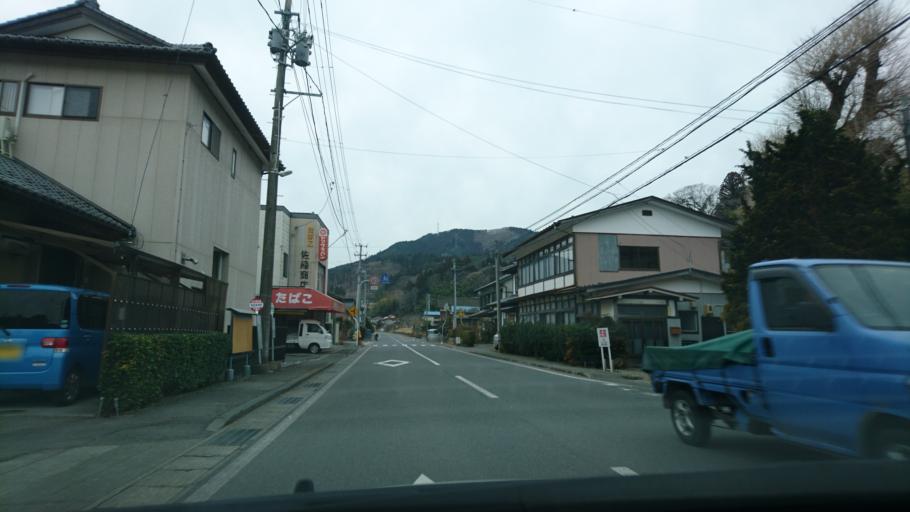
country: JP
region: Iwate
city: Ofunato
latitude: 39.1473
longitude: 141.5726
